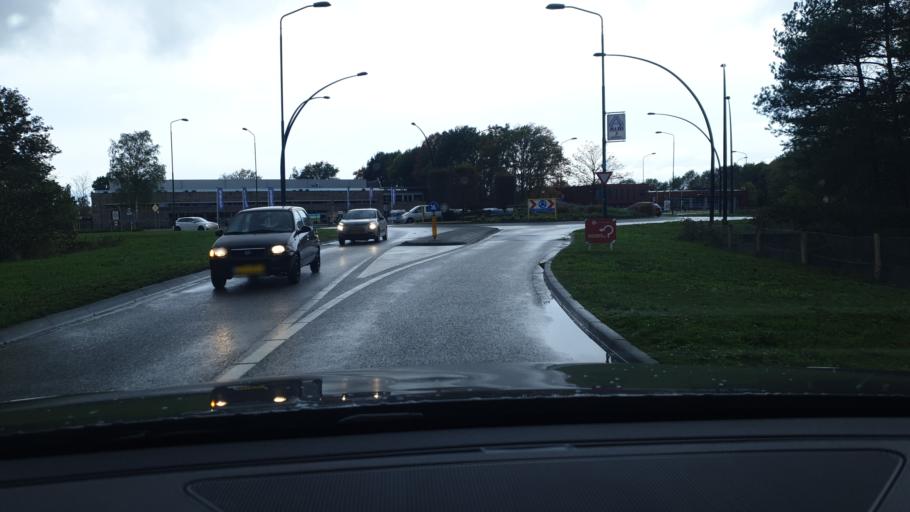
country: NL
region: North Brabant
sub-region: Gemeente Bernheze
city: Heesch
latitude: 51.7145
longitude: 5.5589
